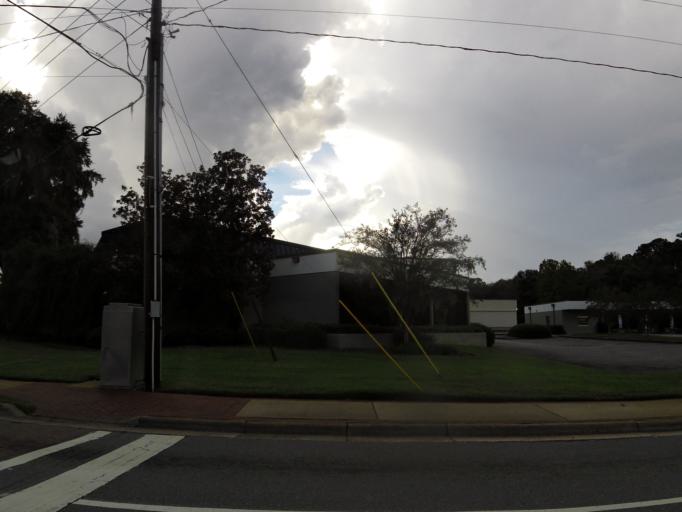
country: US
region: Georgia
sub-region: Liberty County
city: Hinesville
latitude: 31.8441
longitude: -81.5971
